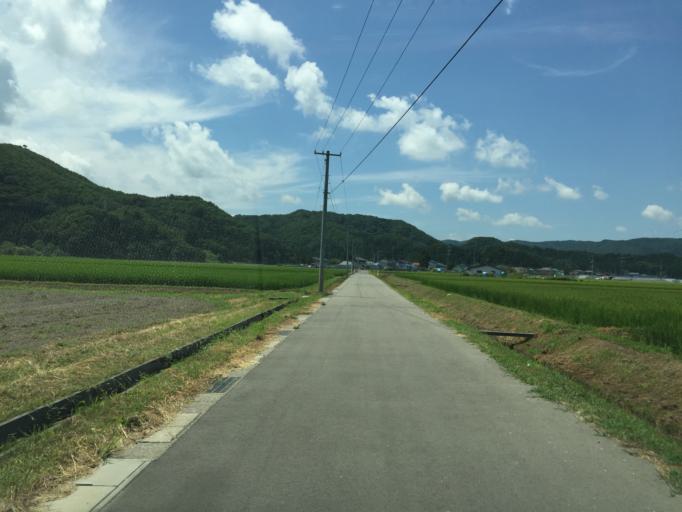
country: JP
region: Fukushima
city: Inawashiro
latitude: 37.4509
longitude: 140.0476
